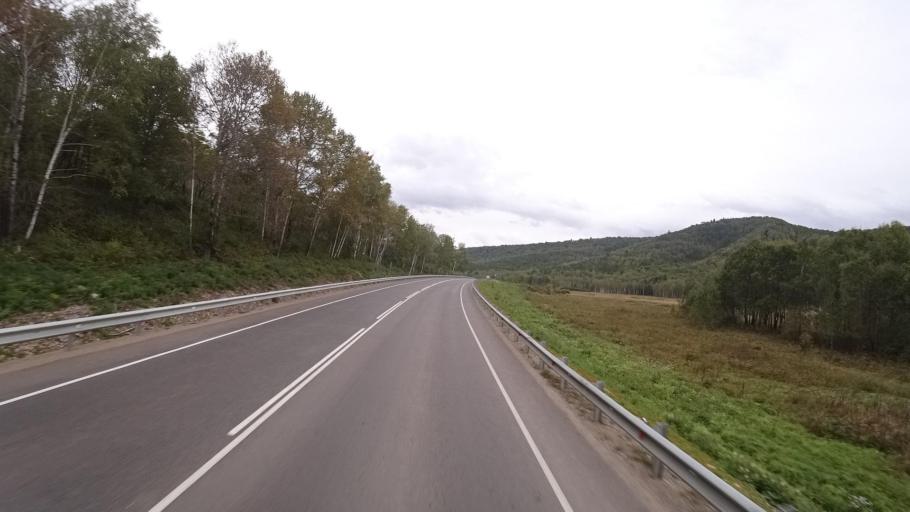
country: RU
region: Jewish Autonomous Oblast
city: Khingansk
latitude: 48.9837
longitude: 131.1578
